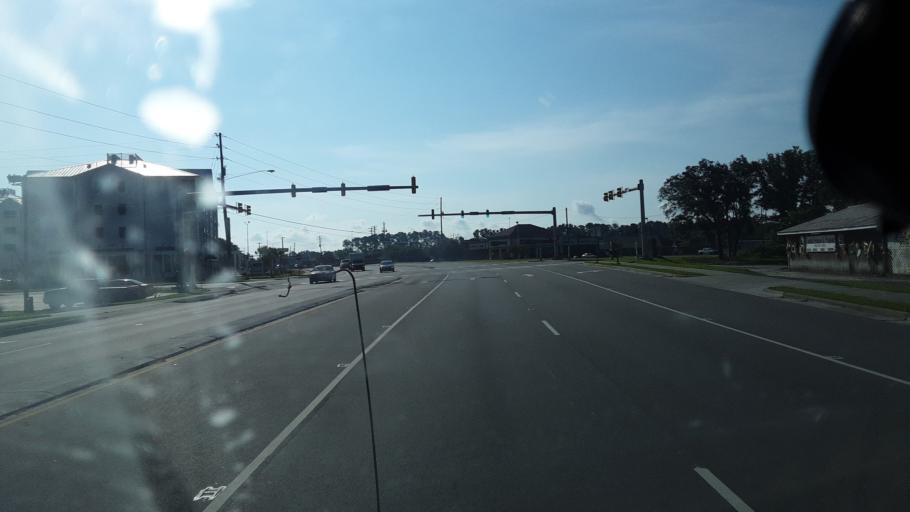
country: US
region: North Carolina
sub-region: Brunswick County
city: Navassa
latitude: 34.2350
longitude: -78.0017
